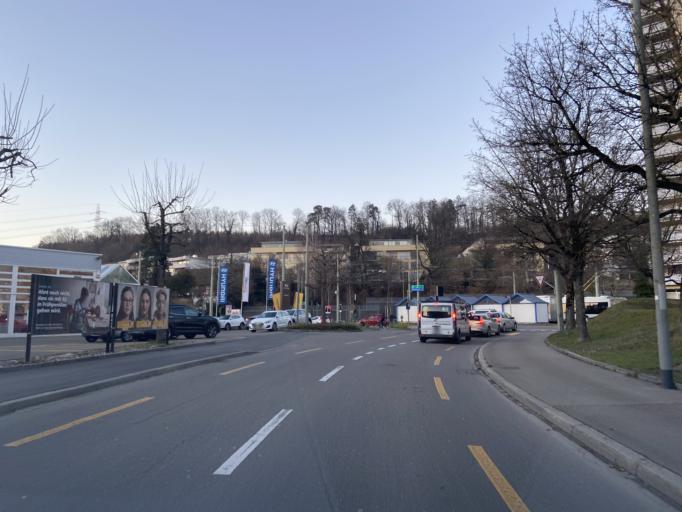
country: CH
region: Zurich
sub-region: Bezirk Winterthur
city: Wuelflingen (Kreis 6) / Haerti
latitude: 47.5144
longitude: 8.6828
